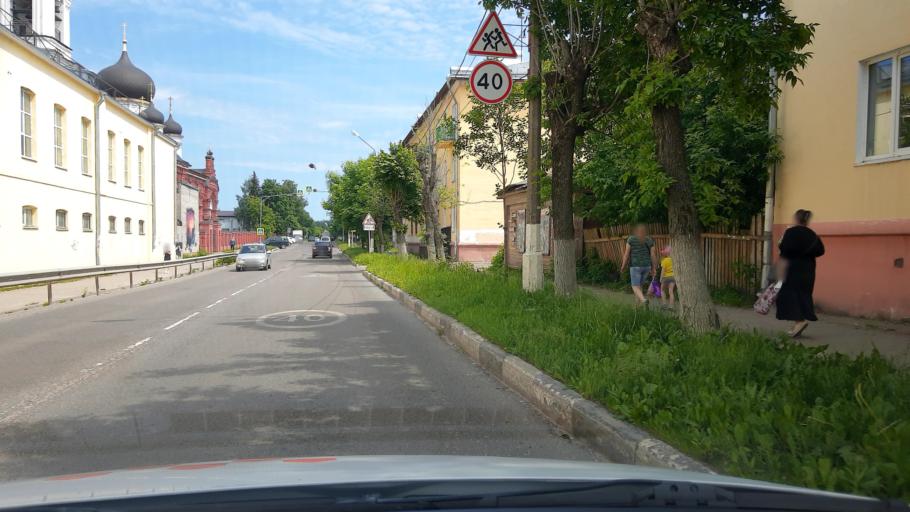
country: RU
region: Moskovskaya
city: Noginsk
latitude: 55.8587
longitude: 38.4445
